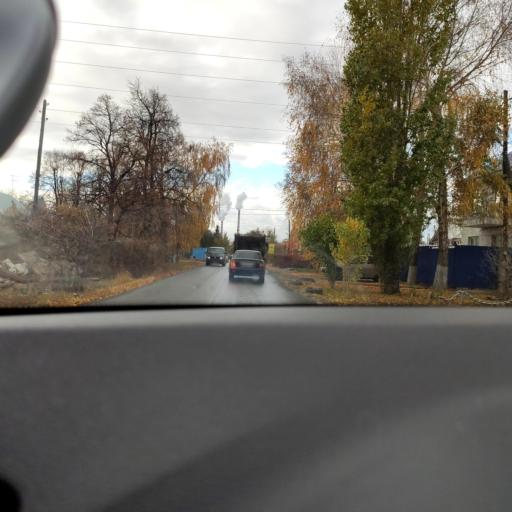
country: RU
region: Samara
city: Petra-Dubrava
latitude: 53.2487
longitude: 50.3195
